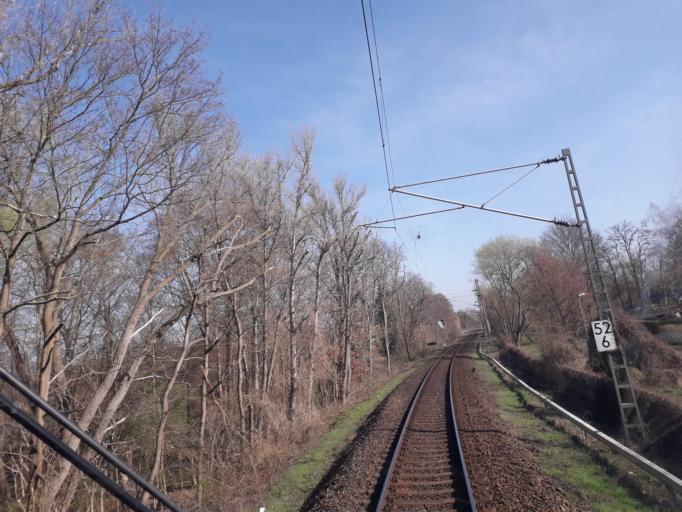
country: DE
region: Brandenburg
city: Werder
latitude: 52.3466
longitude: 12.9813
